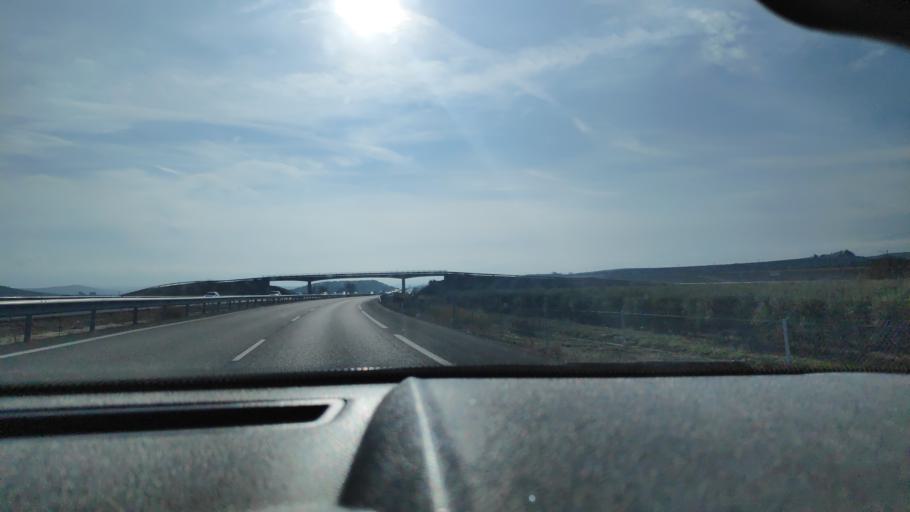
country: ES
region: Andalusia
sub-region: Provincia de Jaen
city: Mengibar
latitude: 37.8824
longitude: -3.7722
